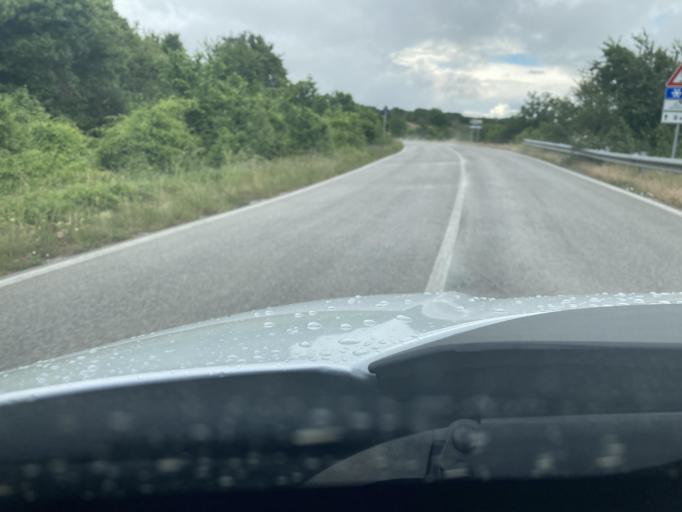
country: IT
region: Abruzzo
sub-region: Provincia dell' Aquila
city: Villa Sant'Angelo
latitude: 42.2399
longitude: 13.5257
